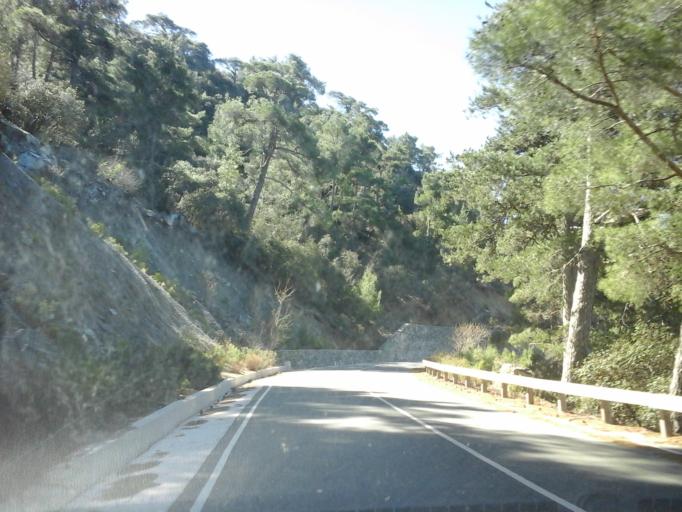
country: CY
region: Lefkosia
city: Kakopetria
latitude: 34.9170
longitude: 32.8330
